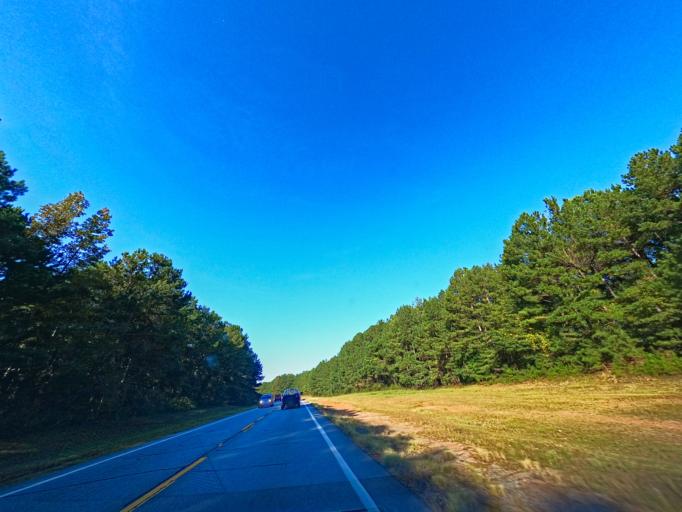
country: US
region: Georgia
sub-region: Coweta County
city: Newnan
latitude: 33.3935
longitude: -84.8351
